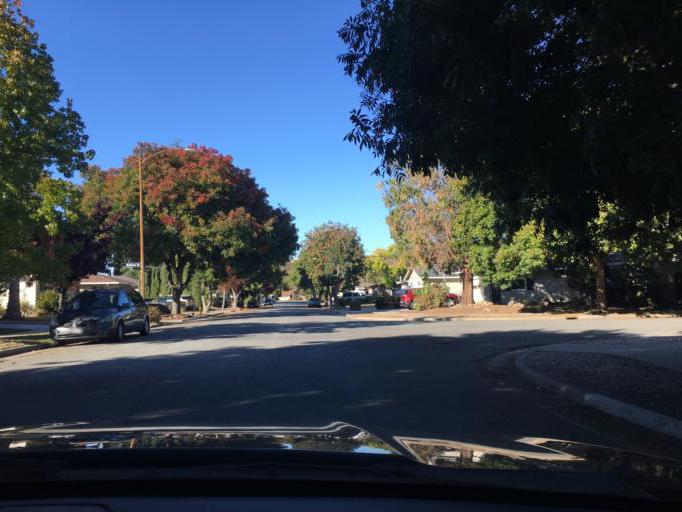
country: US
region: California
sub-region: Santa Clara County
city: Seven Trees
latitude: 37.2273
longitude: -121.8669
